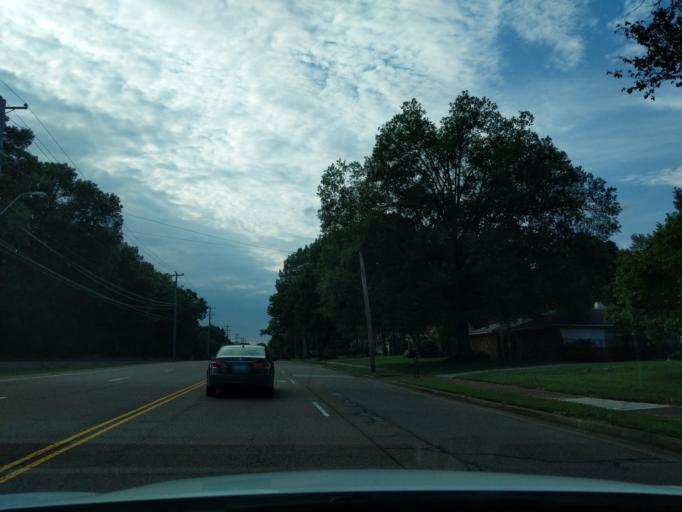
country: US
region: Tennessee
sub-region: Shelby County
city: Germantown
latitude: 35.0768
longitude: -89.7973
